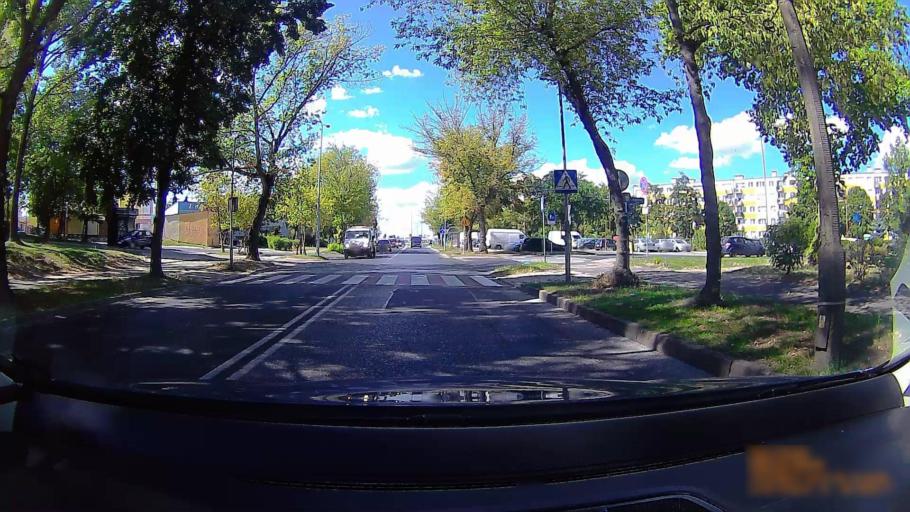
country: PL
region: Greater Poland Voivodeship
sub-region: Konin
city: Konin
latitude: 52.2308
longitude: 18.2798
